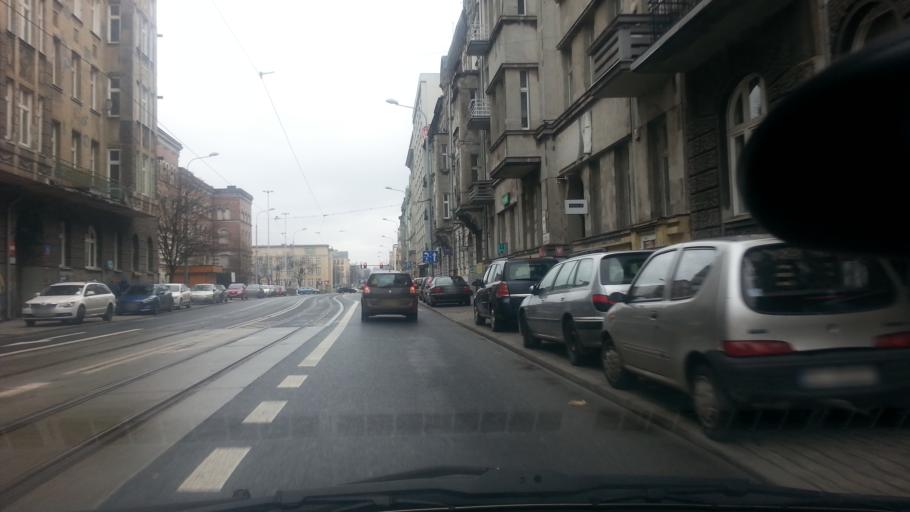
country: PL
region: Lodz Voivodeship
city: Lodz
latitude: 51.7716
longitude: 19.4672
